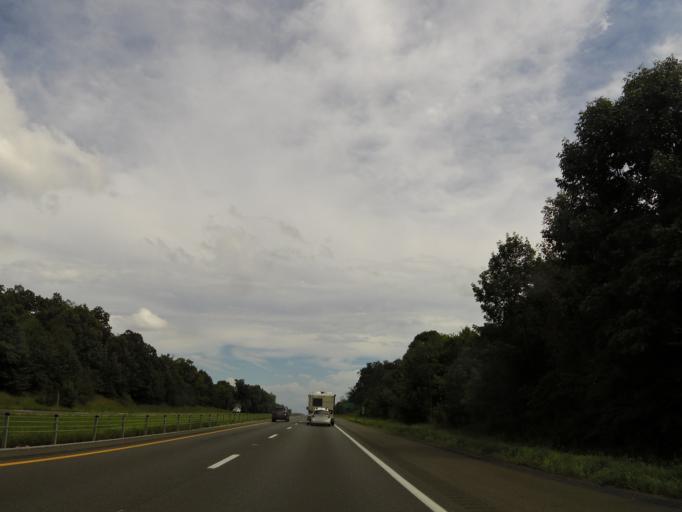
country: US
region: Kentucky
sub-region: McCracken County
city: Hendron
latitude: 37.0439
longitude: -88.6434
